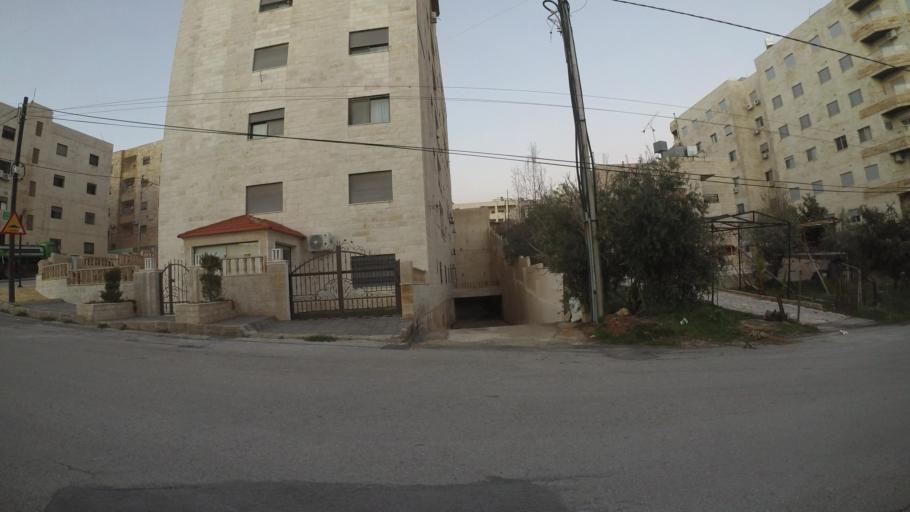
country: JO
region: Amman
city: Al Jubayhah
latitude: 31.9977
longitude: 35.8546
